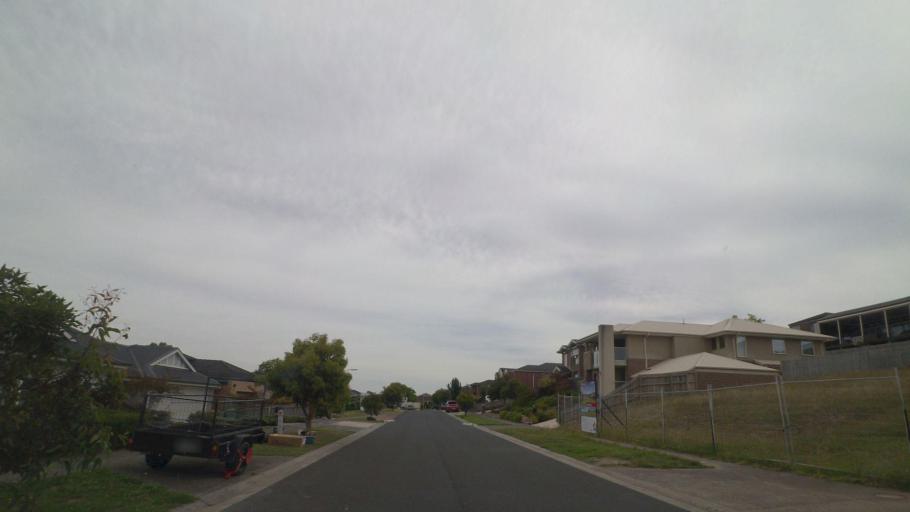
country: AU
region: Victoria
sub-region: Yarra Ranges
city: Kilsyth
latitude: -37.7840
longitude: 145.3415
